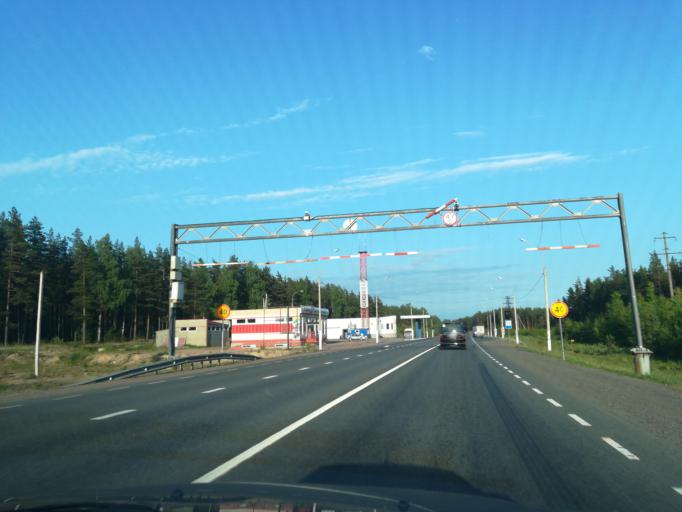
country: RU
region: Leningrad
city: Vyborg
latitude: 60.6647
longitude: 28.9289
